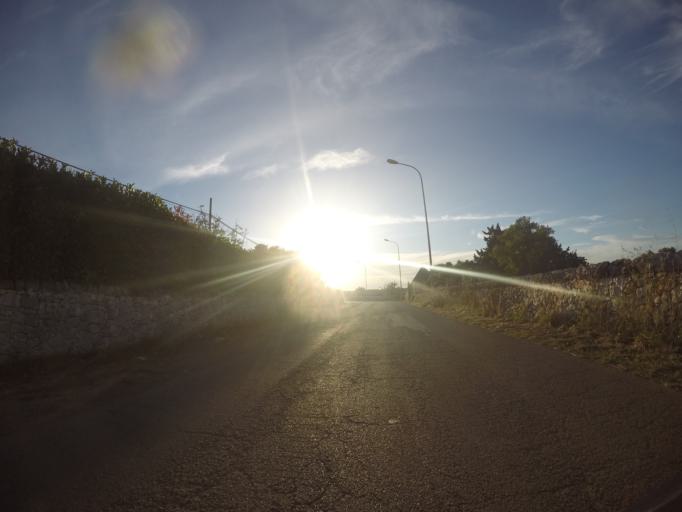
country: IT
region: Apulia
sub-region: Provincia di Taranto
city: Martina Franca
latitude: 40.6535
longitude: 17.3562
